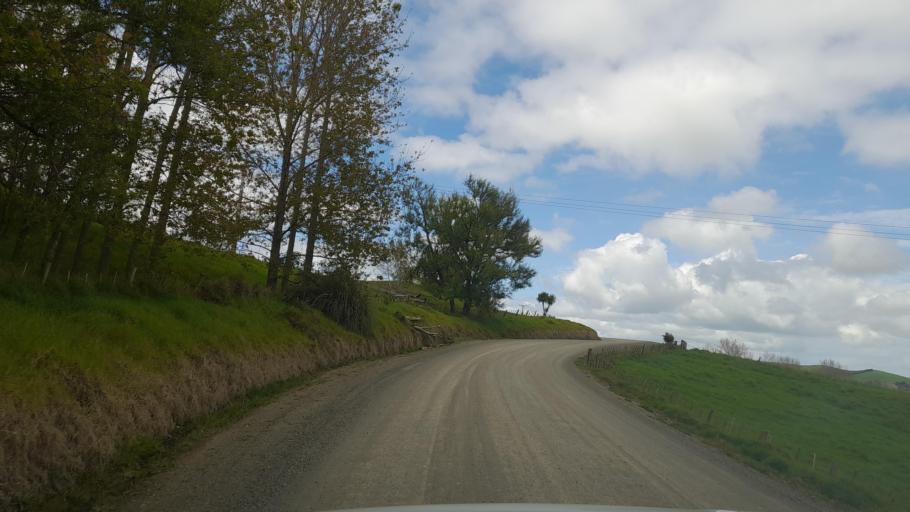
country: NZ
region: Auckland
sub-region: Auckland
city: Wellsford
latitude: -36.1661
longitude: 174.3209
